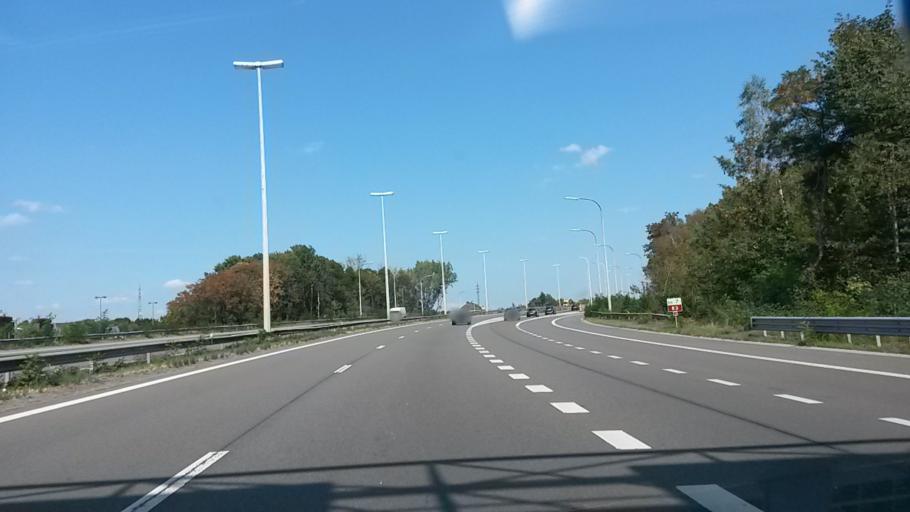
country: BE
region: Wallonia
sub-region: Province du Hainaut
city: Chatelet
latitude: 50.4093
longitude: 4.4977
